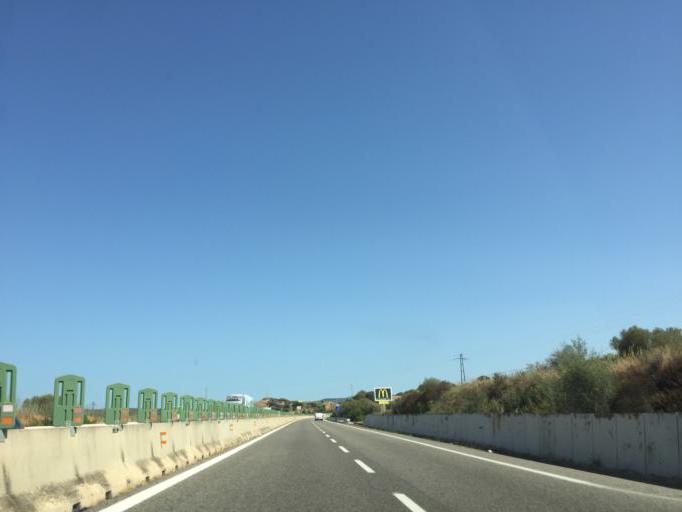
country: IT
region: Sardinia
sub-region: Provincia di Olbia-Tempio
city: Olbia
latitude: 40.8866
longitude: 9.4940
